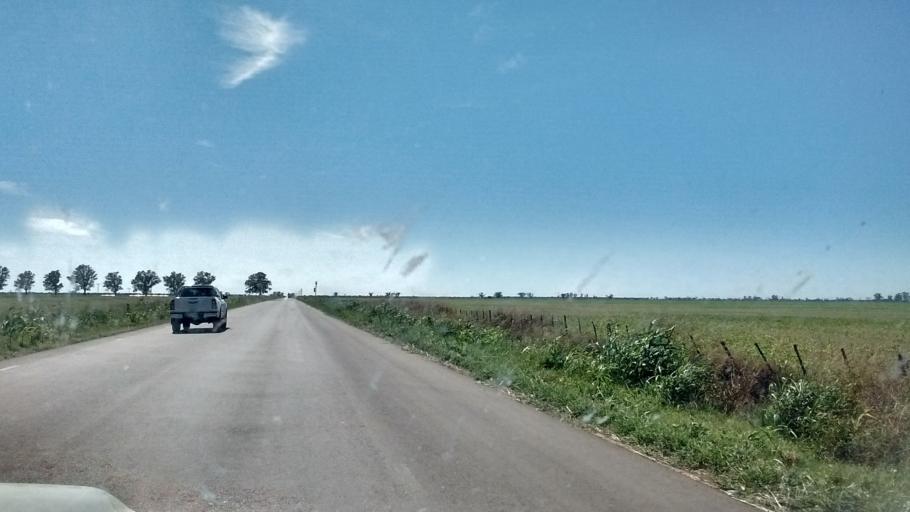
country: AR
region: Cordoba
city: San Francisco
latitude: -31.4353
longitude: -61.9906
